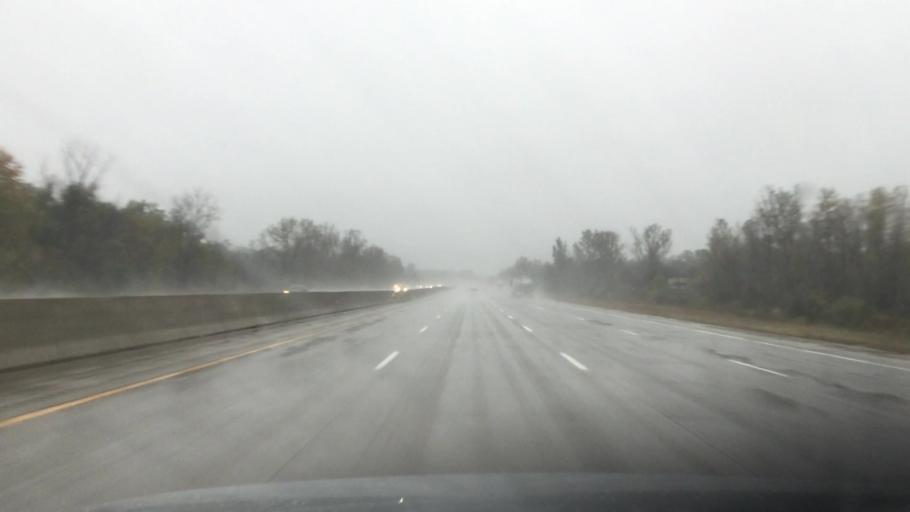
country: US
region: Michigan
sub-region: Saginaw County
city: Birch Run
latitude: 43.2981
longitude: -83.8250
